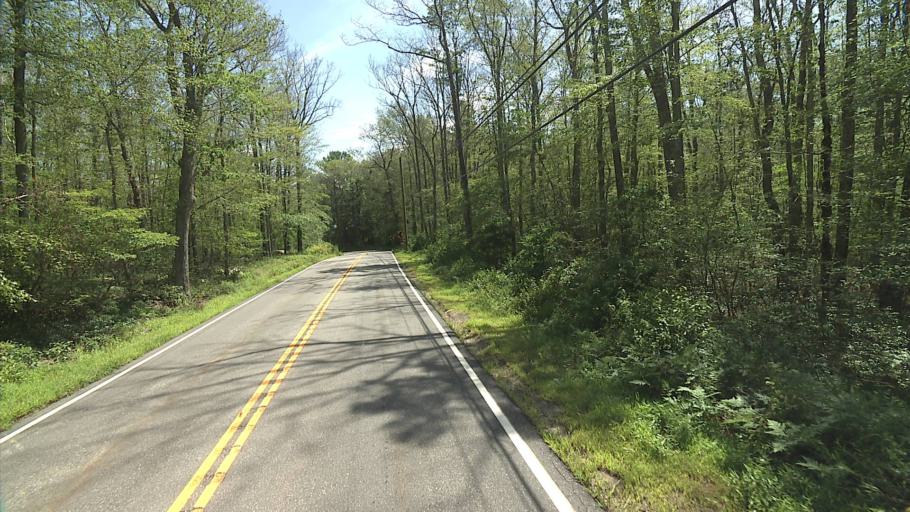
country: US
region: Connecticut
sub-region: Windham County
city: South Woodstock
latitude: 41.8985
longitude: -72.0187
